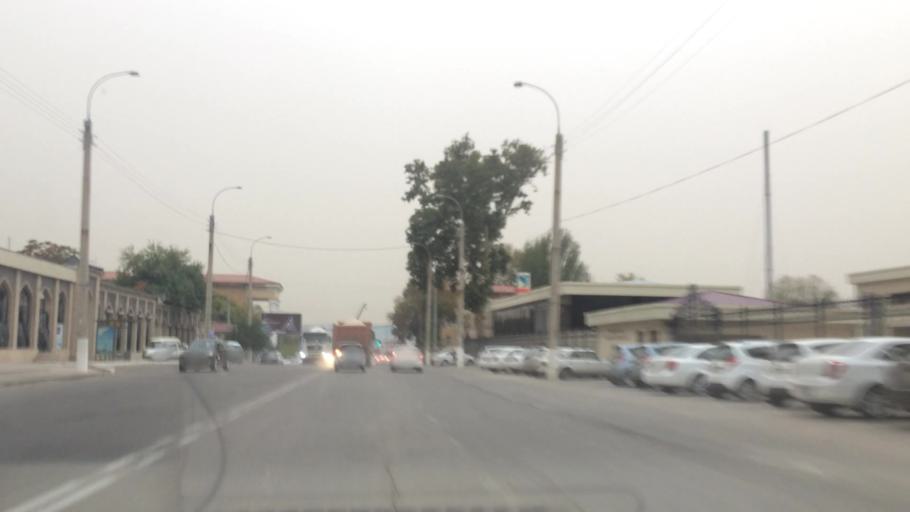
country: UZ
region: Toshkent Shahri
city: Tashkent
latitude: 41.3055
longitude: 69.2498
